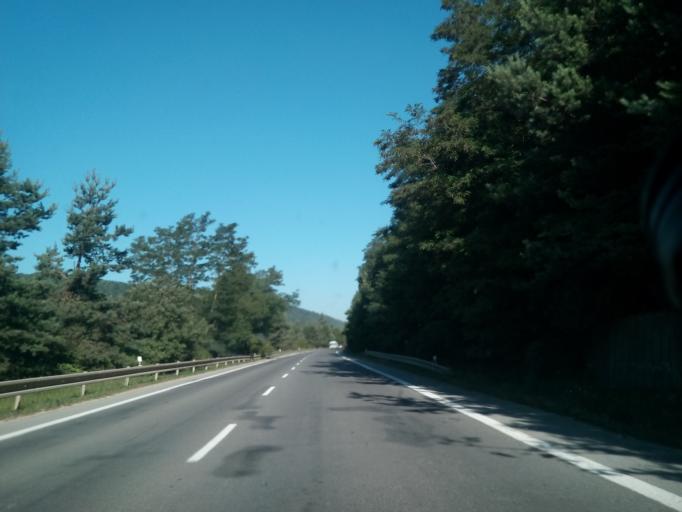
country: SK
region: Presovsky
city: Sabinov
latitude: 49.0107
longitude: 21.0572
